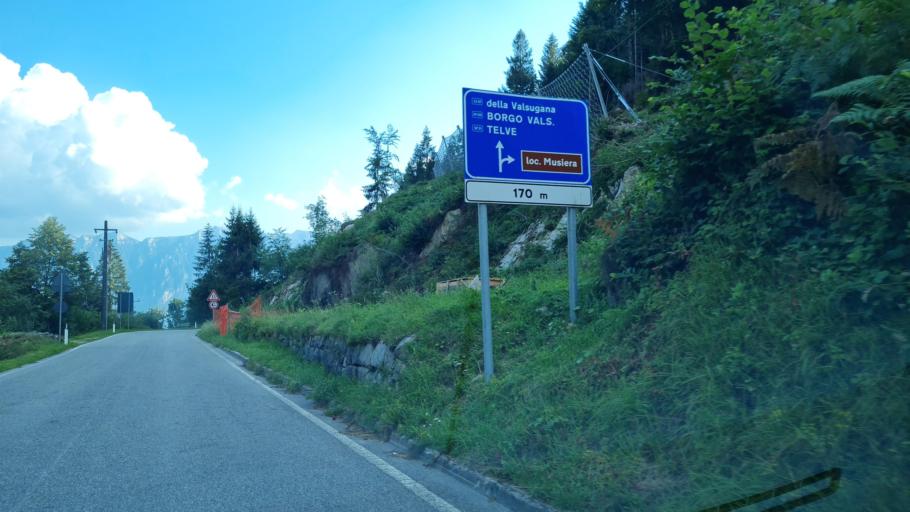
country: IT
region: Trentino-Alto Adige
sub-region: Provincia di Trento
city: Samone
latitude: 46.1055
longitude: 11.5007
